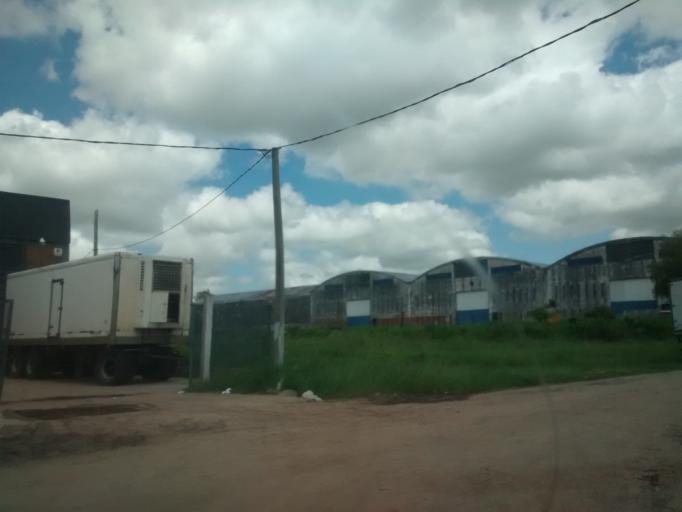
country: AR
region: Chaco
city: Fontana
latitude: -27.4140
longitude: -58.9978
